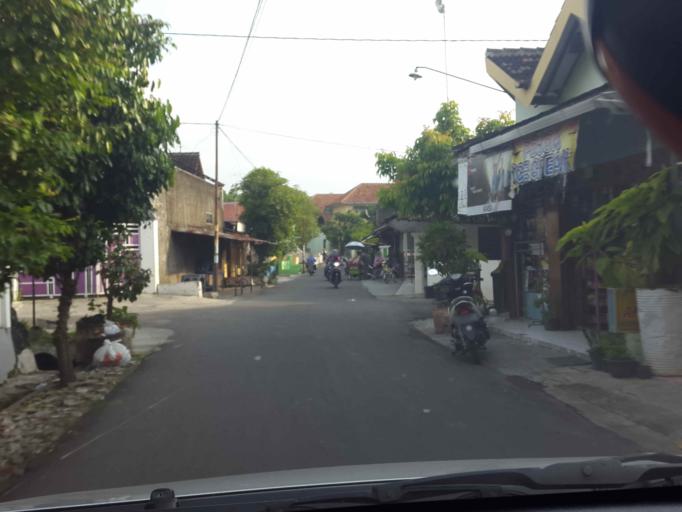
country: ID
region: Central Java
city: Sragen
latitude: -7.4226
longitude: 111.0176
